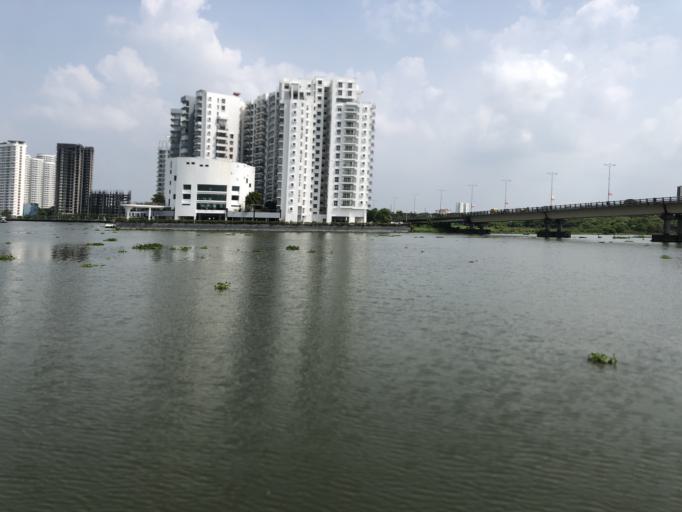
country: IN
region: Kerala
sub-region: Ernakulam
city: Cochin
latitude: 9.9930
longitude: 76.2667
